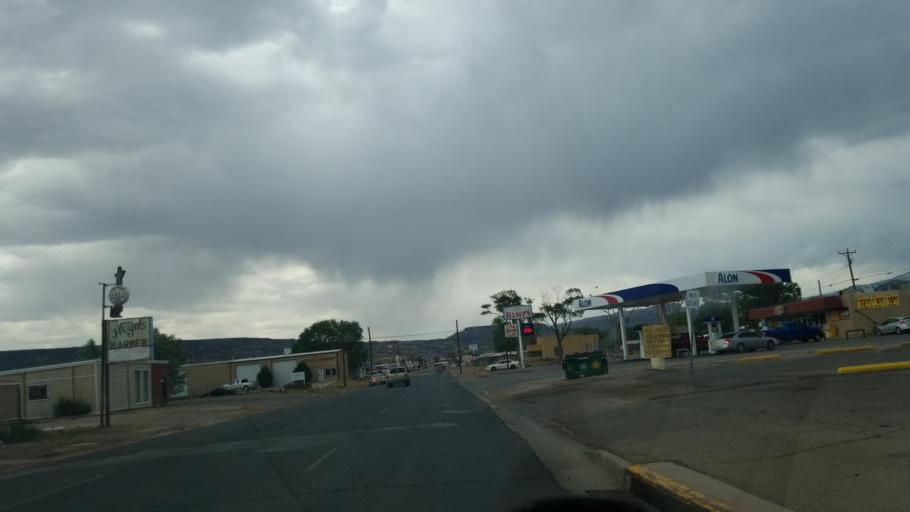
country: US
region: New Mexico
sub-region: Cibola County
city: Grants
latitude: 35.1553
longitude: -107.8455
